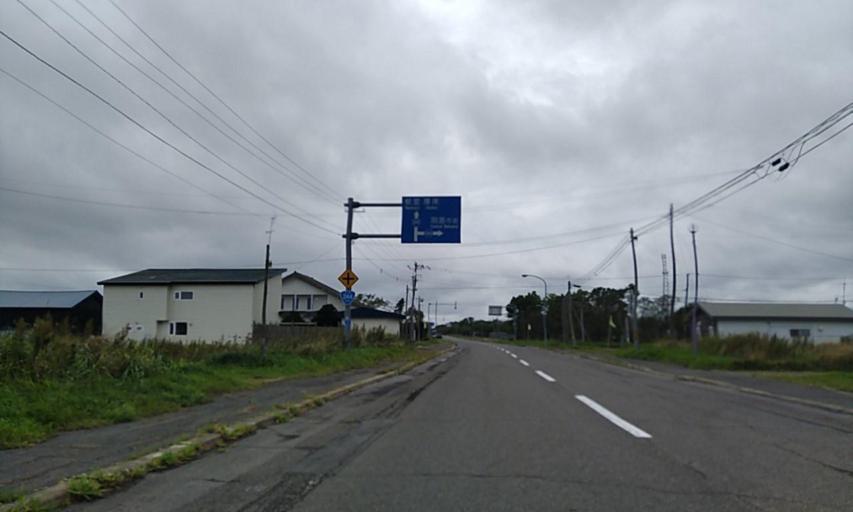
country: JP
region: Hokkaido
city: Nemuro
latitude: 43.3848
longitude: 145.2867
